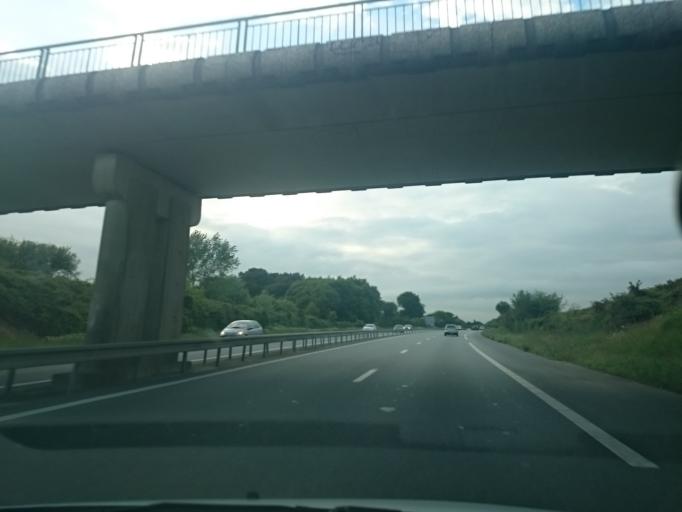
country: FR
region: Brittany
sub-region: Departement du Morbihan
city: Auray
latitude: 47.6734
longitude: -3.0161
